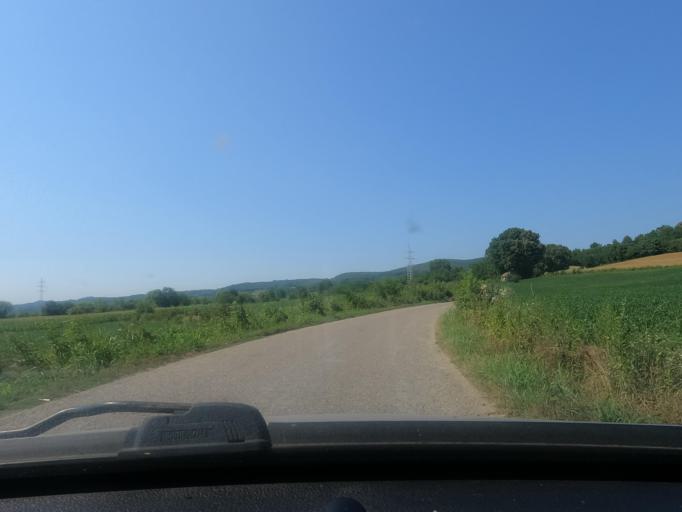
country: RS
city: Jarebice
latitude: 44.5380
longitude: 19.3710
